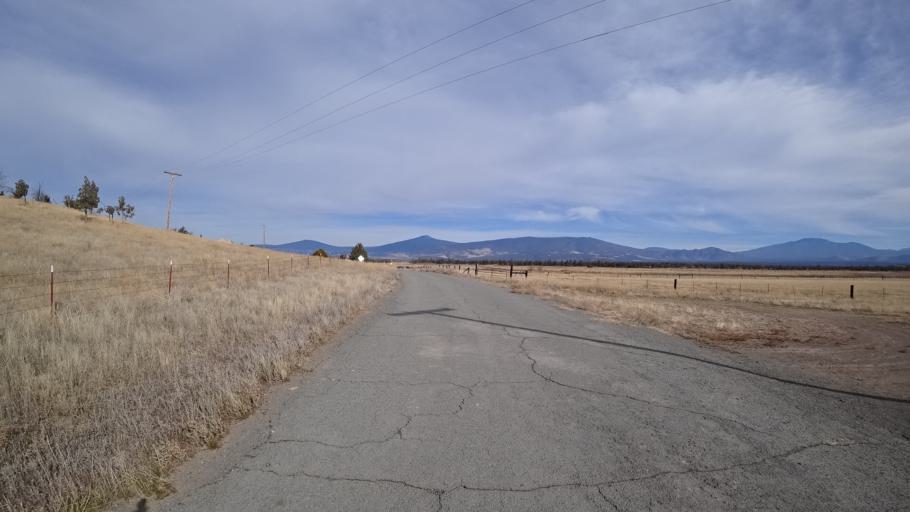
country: US
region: California
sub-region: Siskiyou County
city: Montague
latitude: 41.5923
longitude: -122.4331
